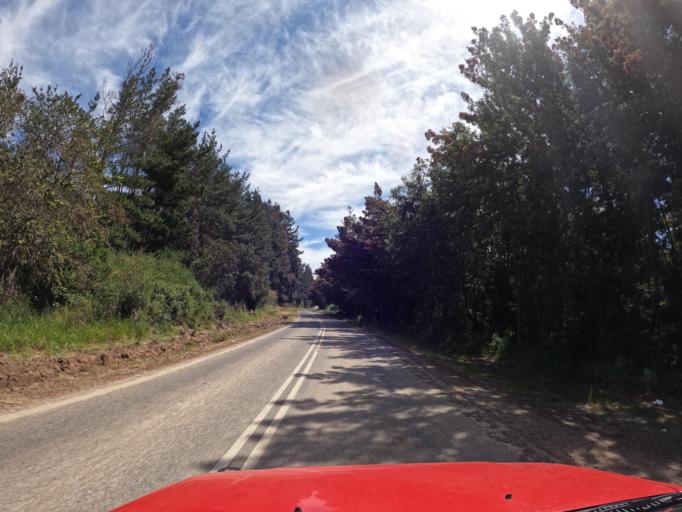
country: CL
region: Maule
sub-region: Provincia de Talca
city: Talca
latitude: -34.9923
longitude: -71.8683
